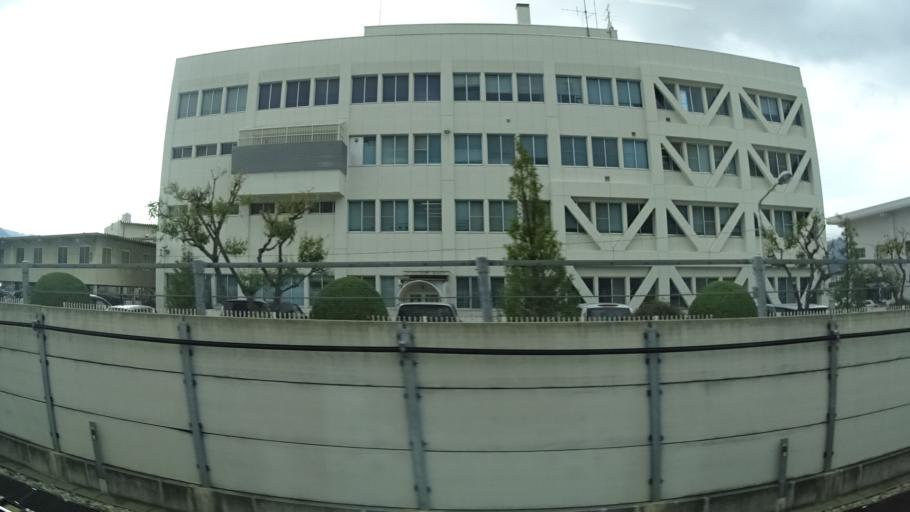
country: JP
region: Nagano
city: Nagano-shi
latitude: 36.6563
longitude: 138.2082
